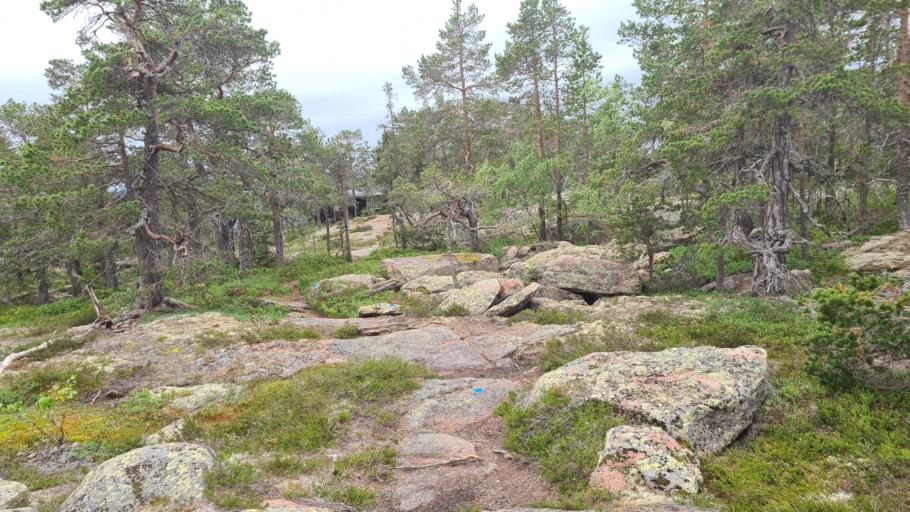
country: SE
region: Vaesternorrland
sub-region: Kramfors Kommun
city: Nordingra
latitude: 62.9741
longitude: 18.4447
